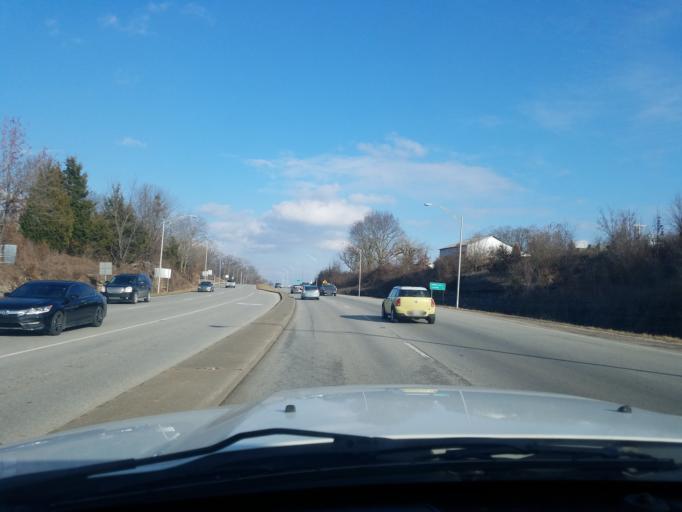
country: US
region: Kentucky
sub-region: Taylor County
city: Campbellsville
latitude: 37.3382
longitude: -85.3598
